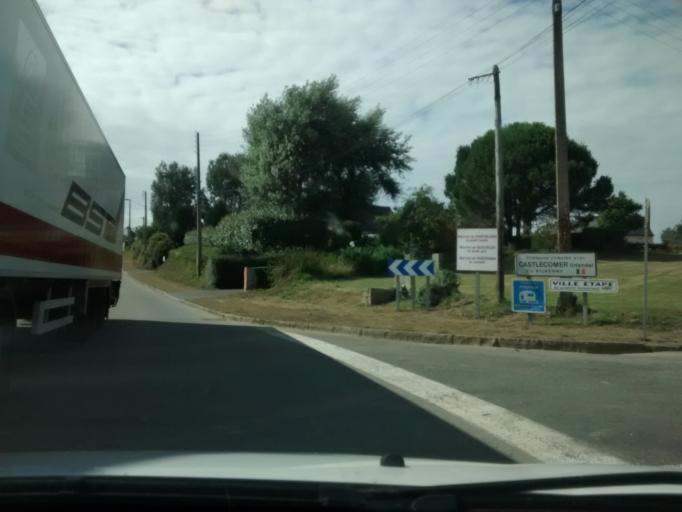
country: FR
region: Brittany
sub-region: Departement des Cotes-d'Armor
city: Penvenan
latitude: 48.8026
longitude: -3.2895
